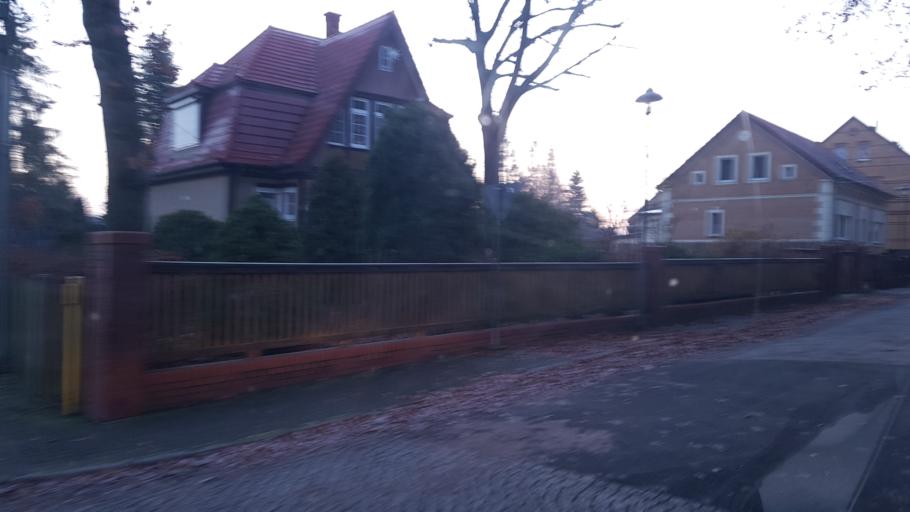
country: DE
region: Brandenburg
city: Schipkau
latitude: 51.5437
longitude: 13.8917
